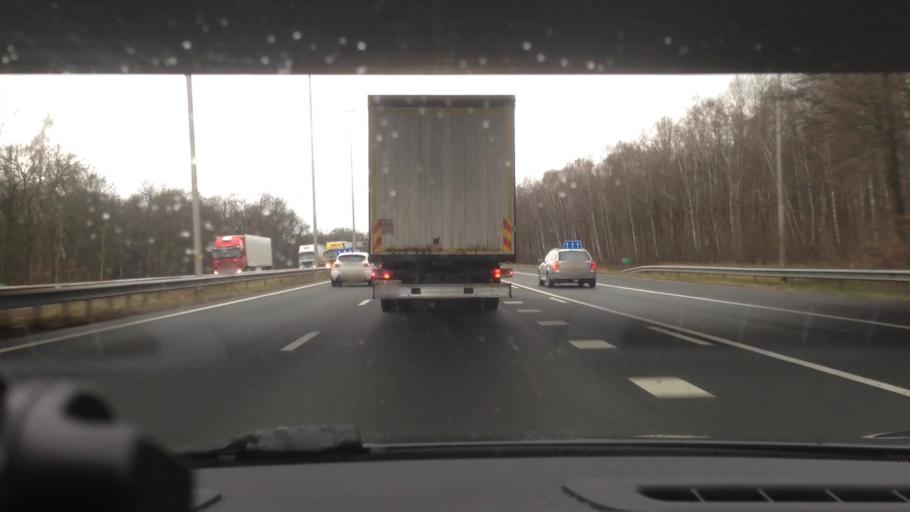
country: NL
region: Overijssel
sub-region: Gemeente Borne
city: Borne
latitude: 52.2927
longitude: 6.7299
